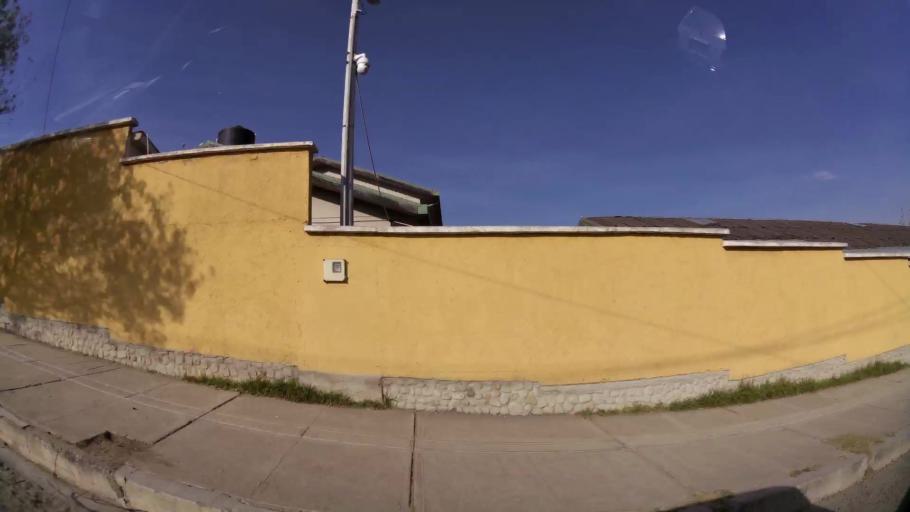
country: BO
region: La Paz
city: La Paz
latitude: -16.5157
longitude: -68.0846
